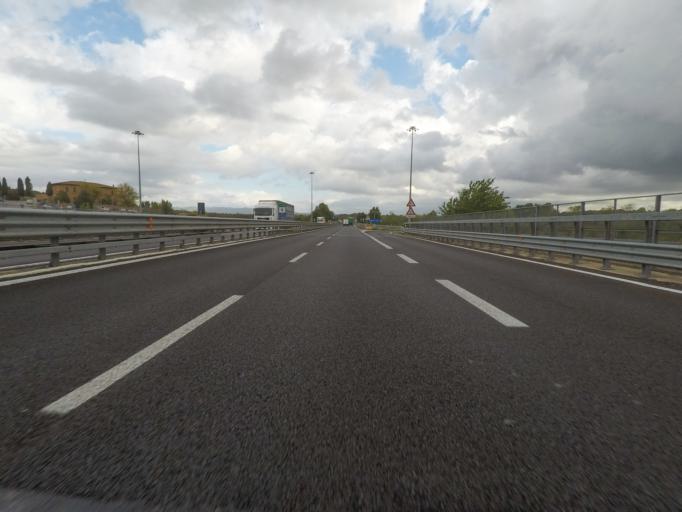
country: IT
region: Tuscany
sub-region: Provincia di Siena
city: Arbia
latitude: 43.2987
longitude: 11.4030
